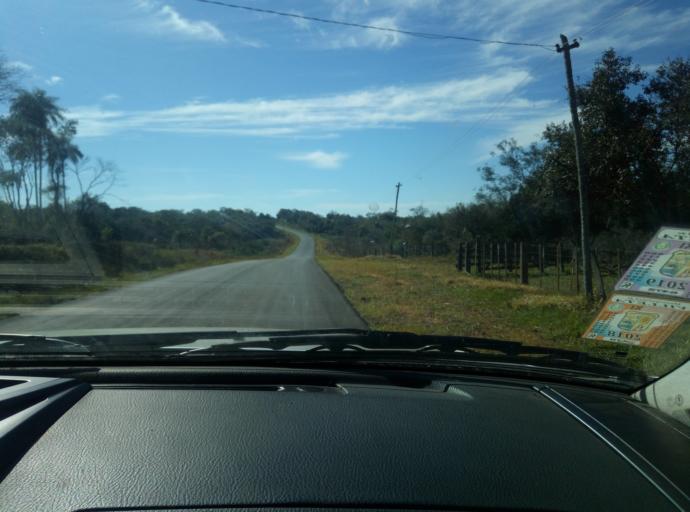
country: PY
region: Caaguazu
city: Carayao
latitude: -25.1737
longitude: -56.3134
